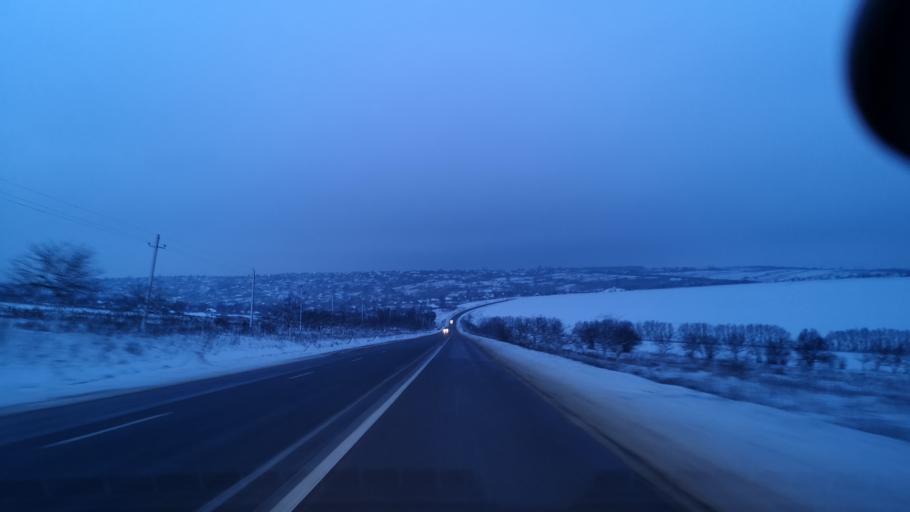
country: MD
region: Soldanesti
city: Soldanesti
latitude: 47.7126
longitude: 28.8474
